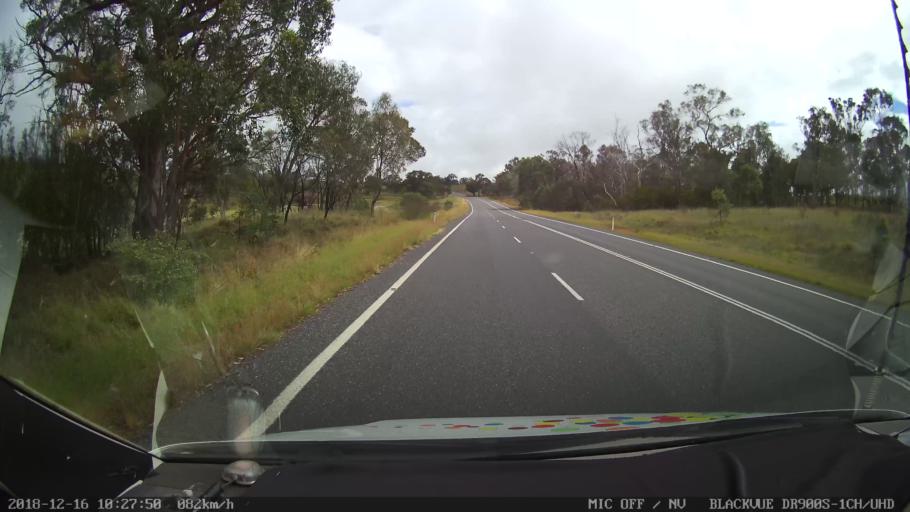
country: AU
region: New South Wales
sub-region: Tenterfield Municipality
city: Carrolls Creek
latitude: -29.1288
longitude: 151.9962
